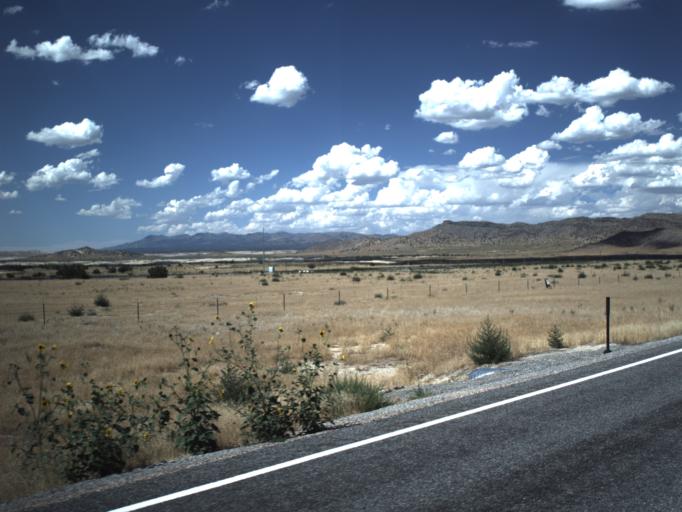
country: US
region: Utah
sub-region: Millard County
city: Delta
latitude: 39.6350
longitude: -112.3073
